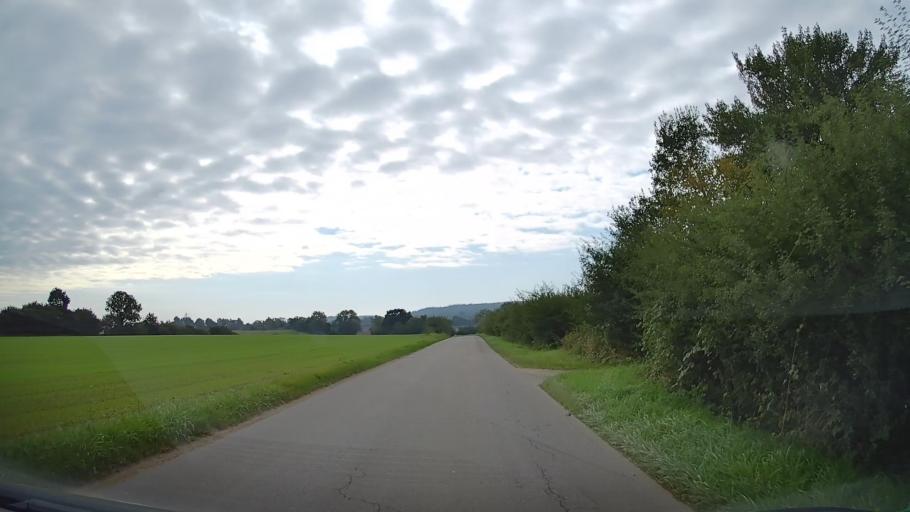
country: DE
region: Schleswig-Holstein
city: Panker
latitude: 54.3552
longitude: 10.5600
